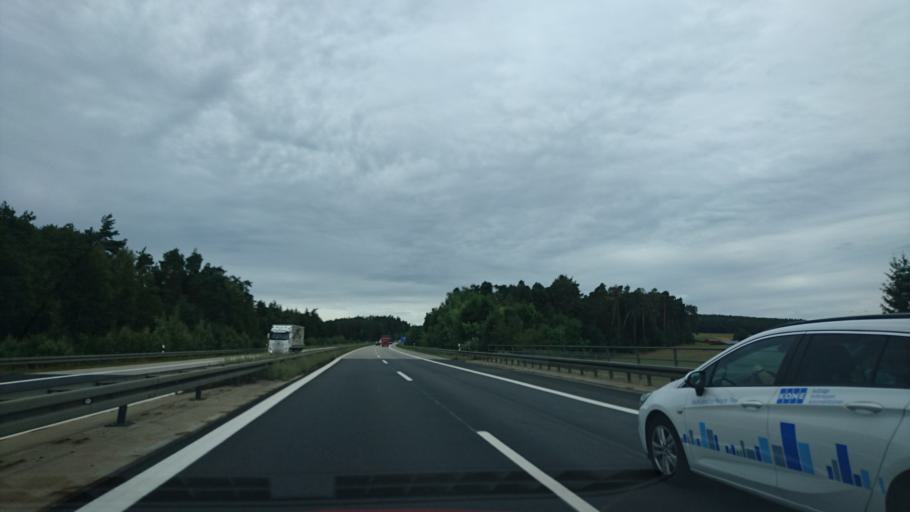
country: DE
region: Bavaria
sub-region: Upper Palatinate
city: Luhe-Wildenau
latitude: 49.5574
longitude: 12.1227
